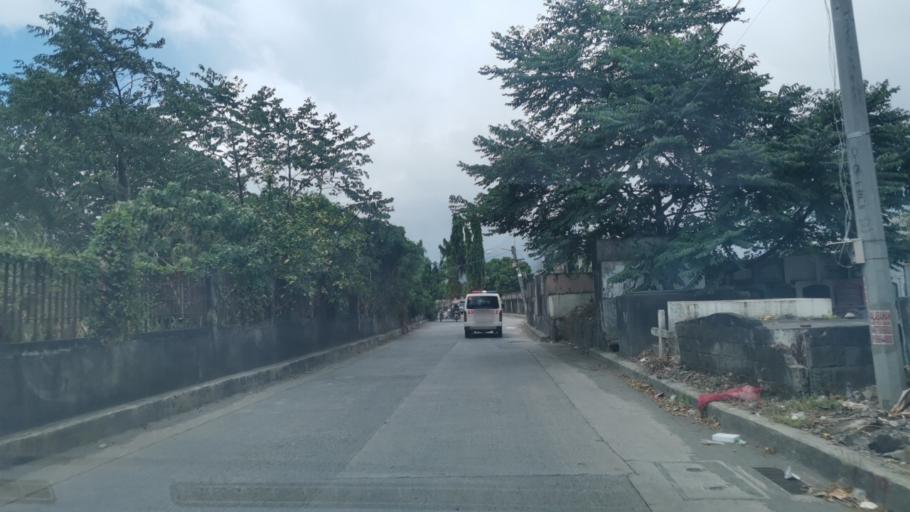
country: PH
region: Calabarzon
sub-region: Province of Batangas
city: Tanauan
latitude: 14.0871
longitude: 121.1389
